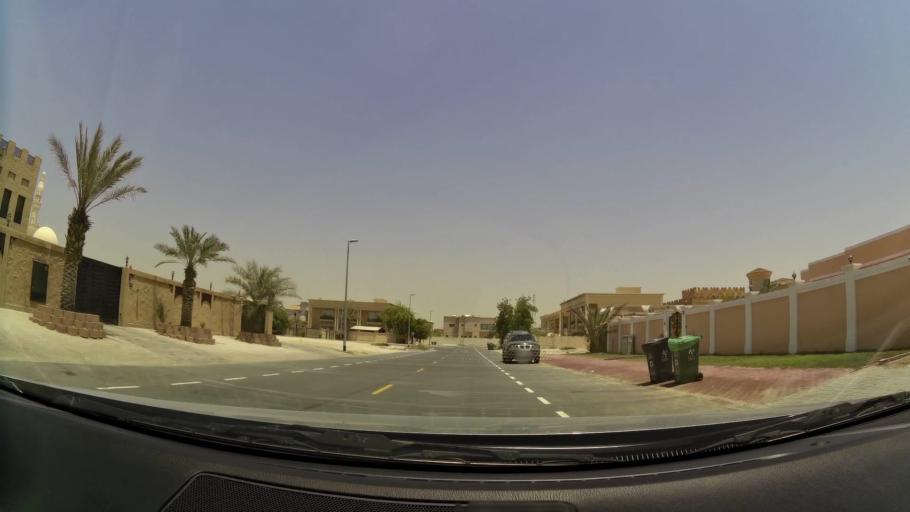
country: AE
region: Dubai
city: Dubai
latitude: 25.0893
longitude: 55.1937
